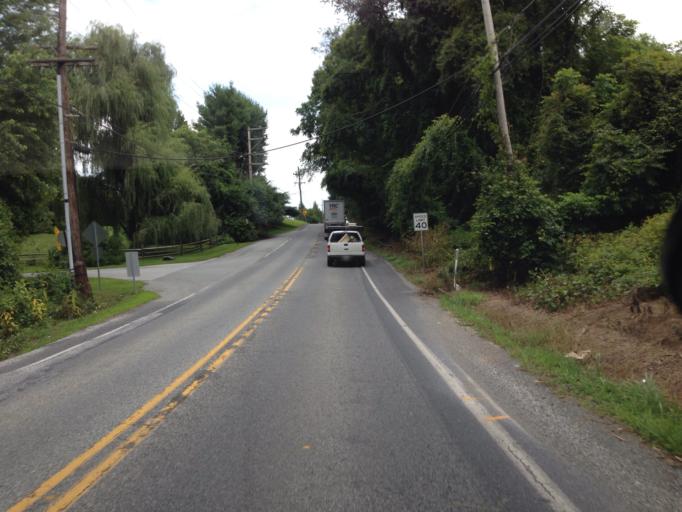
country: US
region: Pennsylvania
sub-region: Chester County
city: West Grove
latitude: 39.7605
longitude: -75.8418
